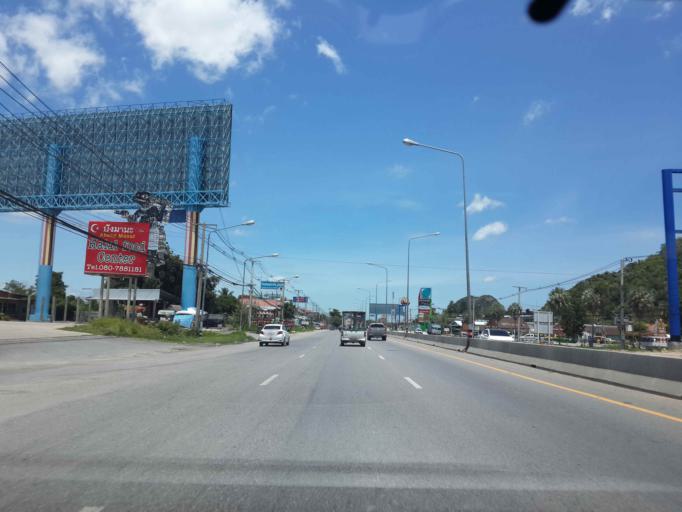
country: TH
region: Phetchaburi
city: Cha-am
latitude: 12.8149
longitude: 99.9416
